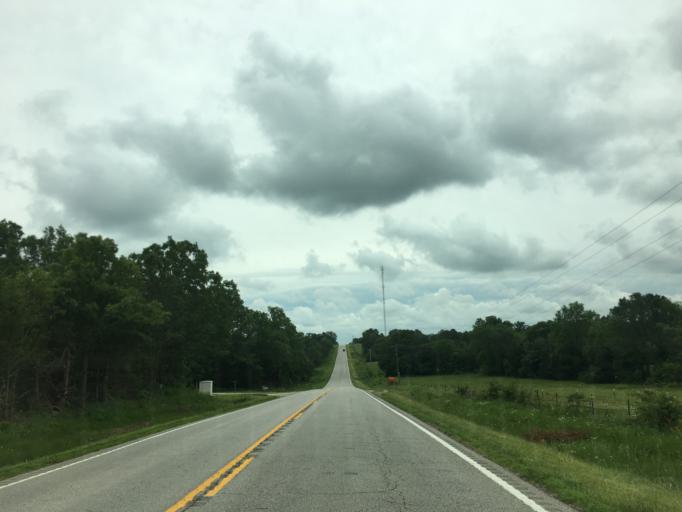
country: US
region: Missouri
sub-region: Gasconade County
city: Owensville
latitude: 38.4960
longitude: -91.4620
